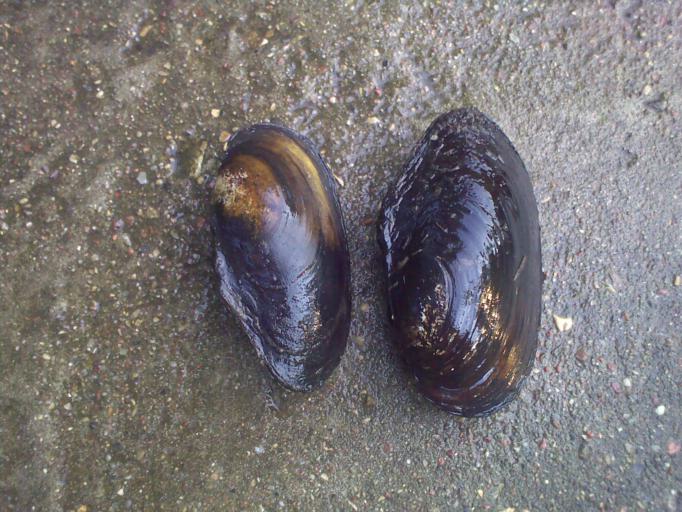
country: PL
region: Masovian Voivodeship
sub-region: Powiat piaseczynski
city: Tarczyn
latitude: 51.9726
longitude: 20.7760
